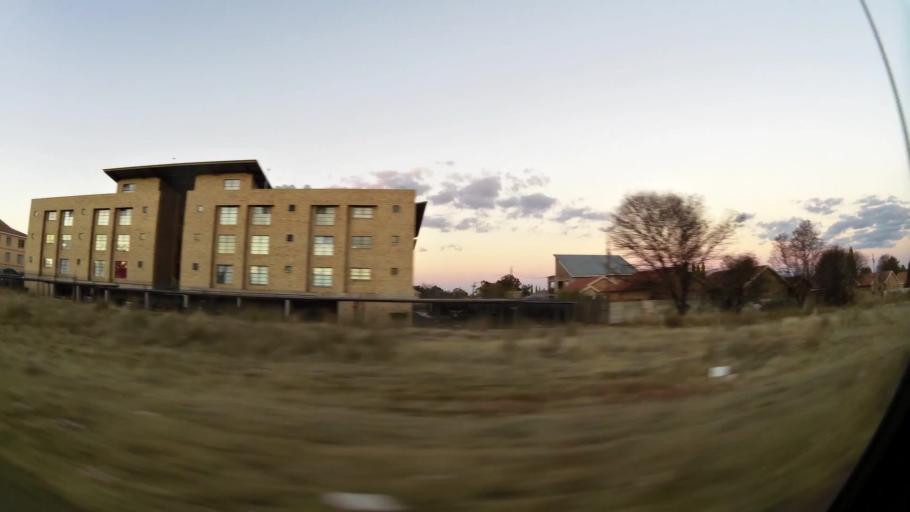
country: ZA
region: North-West
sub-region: Dr Kenneth Kaunda District Municipality
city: Potchefstroom
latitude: -26.6907
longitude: 27.0781
